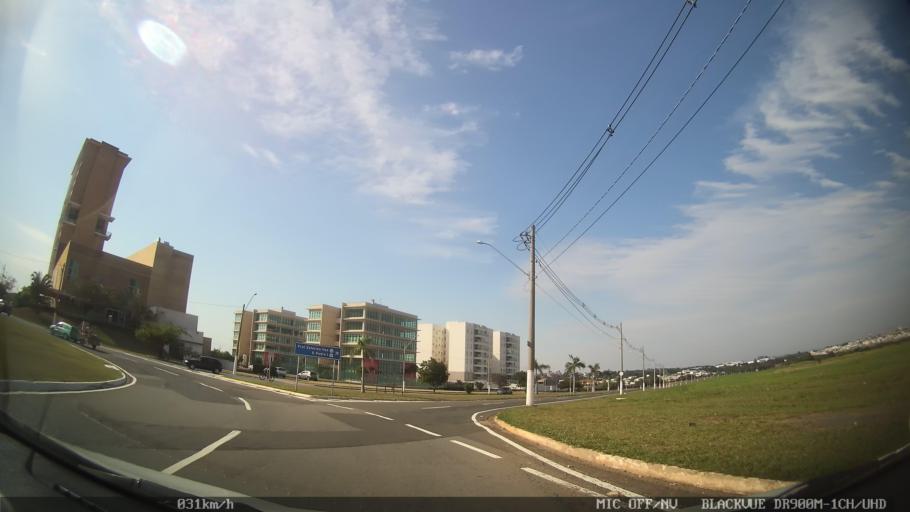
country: BR
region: Sao Paulo
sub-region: Paulinia
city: Paulinia
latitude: -22.7843
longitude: -47.1518
